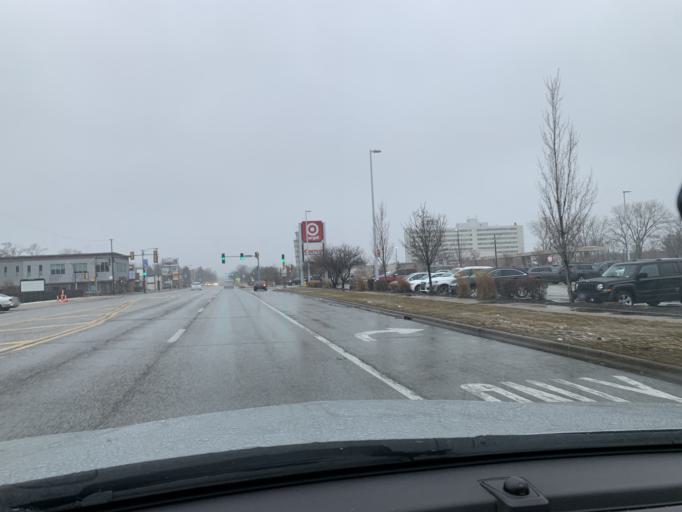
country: US
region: Illinois
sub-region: Cook County
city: Niles
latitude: 42.0120
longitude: -87.7806
